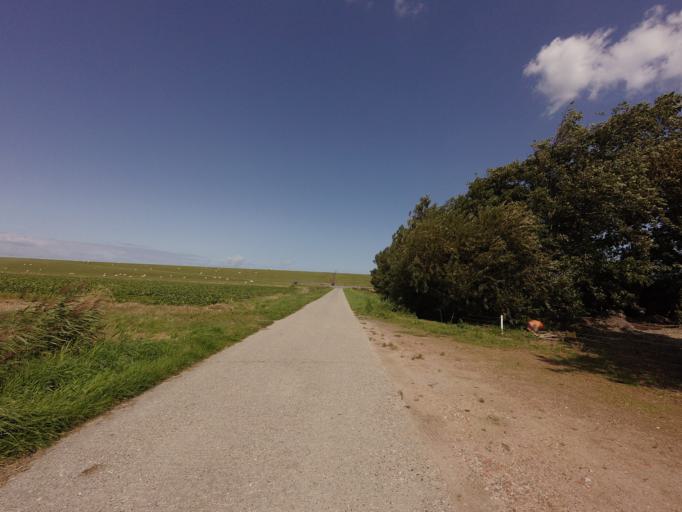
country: NL
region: Friesland
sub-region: Gemeente Ferwerderadiel
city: Hallum
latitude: 53.3230
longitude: 5.7222
